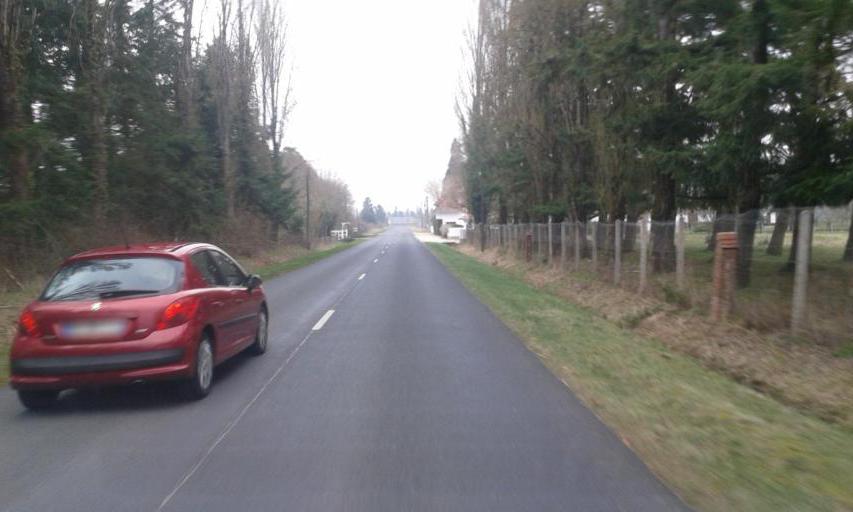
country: FR
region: Centre
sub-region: Departement du Loir-et-Cher
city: Saint-Laurent-Nouan
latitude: 47.7049
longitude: 1.6645
